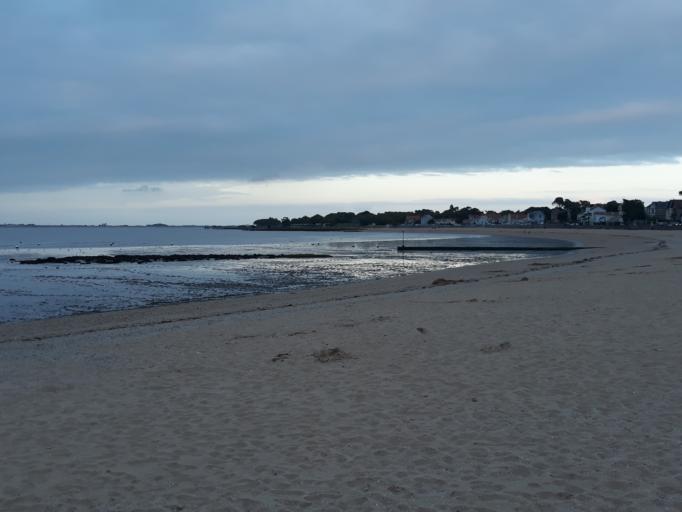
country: FR
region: Poitou-Charentes
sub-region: Departement de la Charente-Maritime
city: Fouras
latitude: 45.9924
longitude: -1.0972
